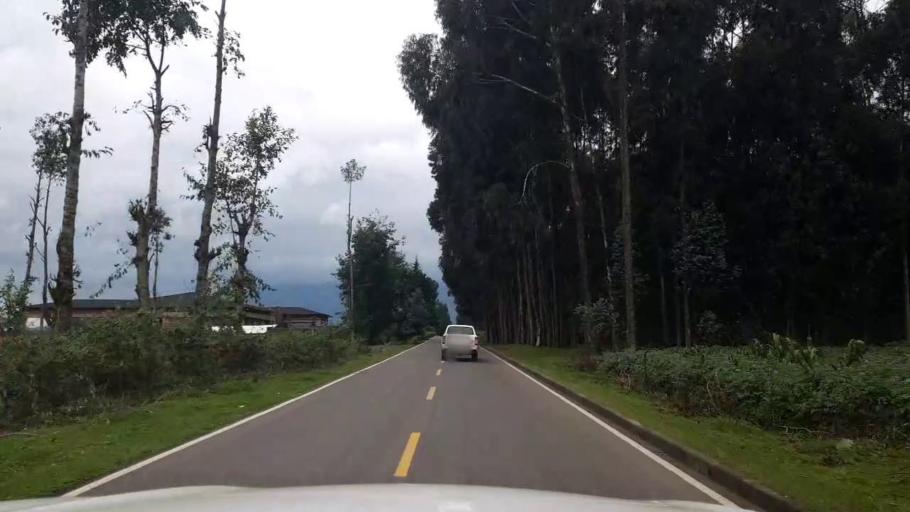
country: RW
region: Northern Province
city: Musanze
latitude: -1.4322
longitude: 29.5591
